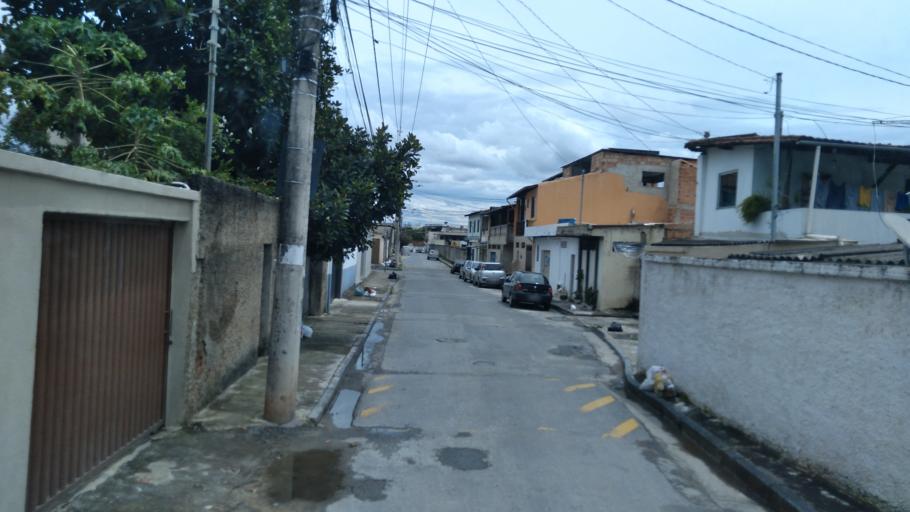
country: BR
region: Minas Gerais
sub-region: Belo Horizonte
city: Belo Horizonte
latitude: -19.8550
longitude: -43.9200
